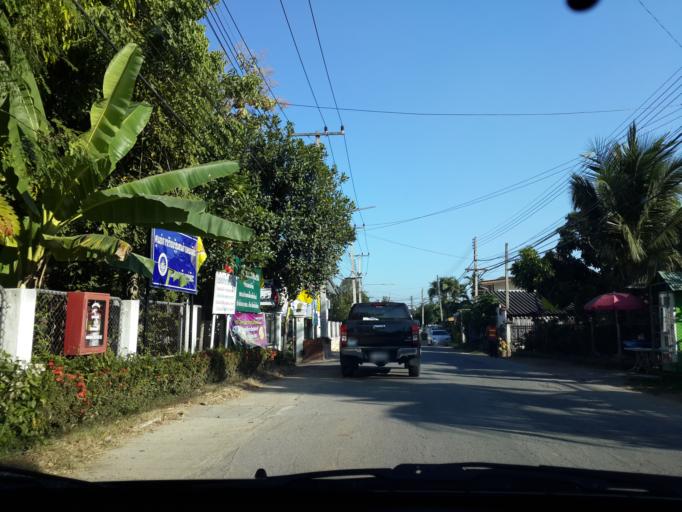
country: TH
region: Chiang Mai
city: Chiang Mai
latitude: 18.7379
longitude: 98.9534
